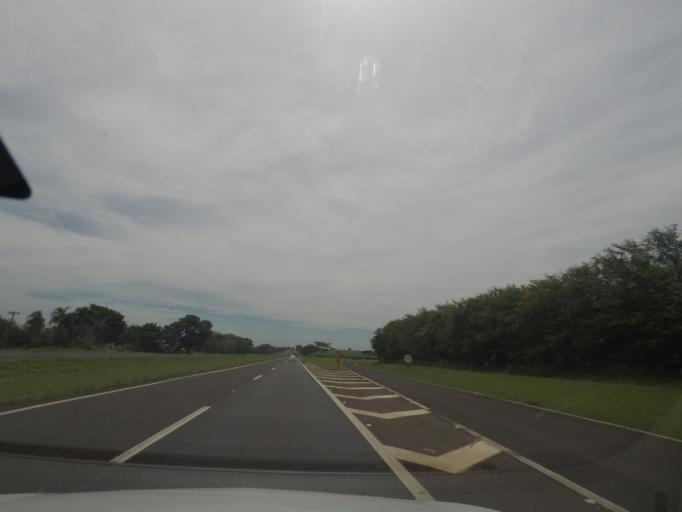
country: BR
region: Sao Paulo
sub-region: Bebedouro
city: Bebedouro
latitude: -20.9642
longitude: -48.4421
